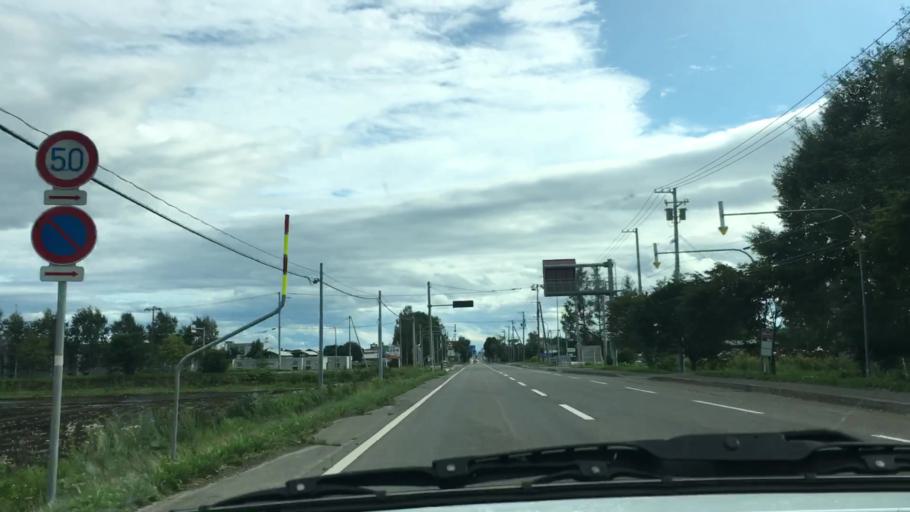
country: JP
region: Hokkaido
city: Otofuke
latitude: 43.2407
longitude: 143.2969
